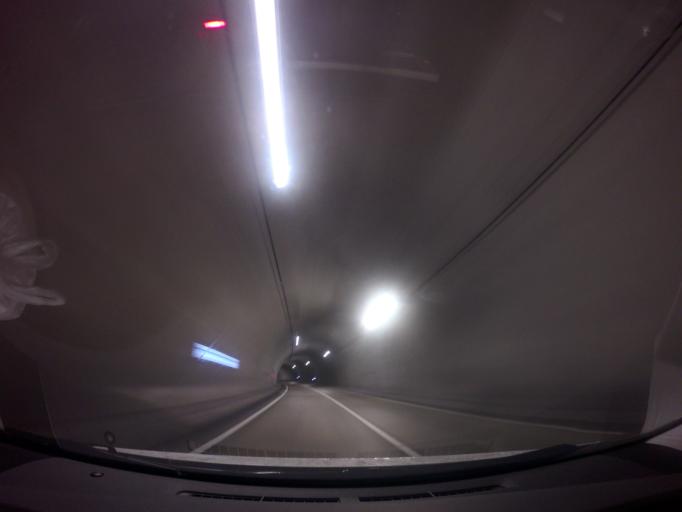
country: JP
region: Wakayama
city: Koya
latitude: 33.9759
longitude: 135.8060
